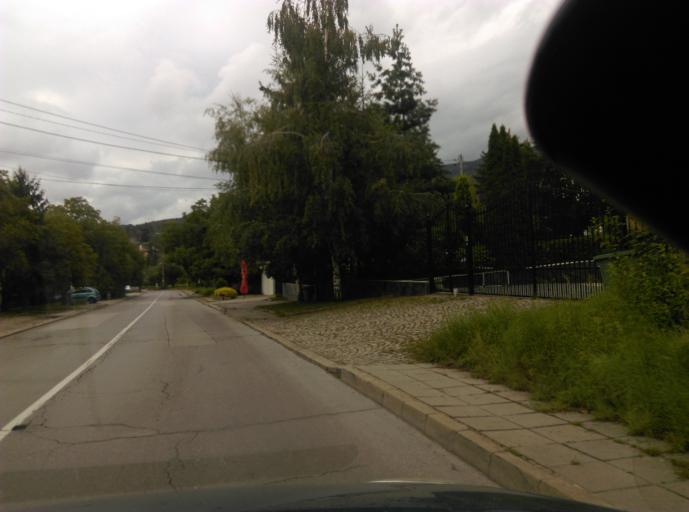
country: BG
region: Sofia-Capital
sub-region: Stolichna Obshtina
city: Sofia
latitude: 42.6246
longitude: 23.3193
